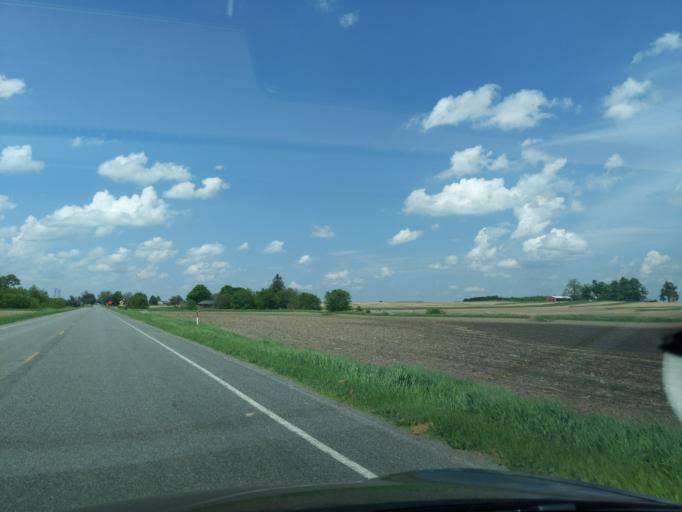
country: US
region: Michigan
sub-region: Ingham County
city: Mason
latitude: 42.6080
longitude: -84.4329
